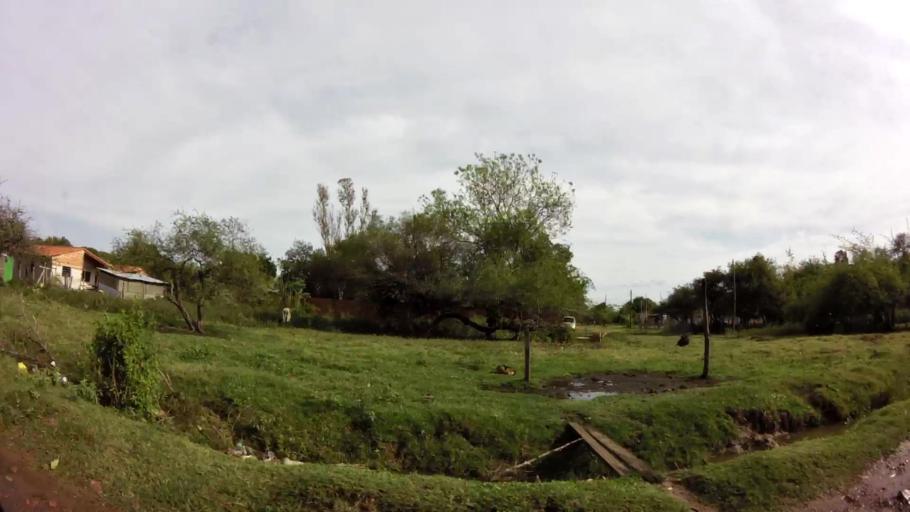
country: PY
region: Central
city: Limpio
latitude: -25.1709
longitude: -57.4900
